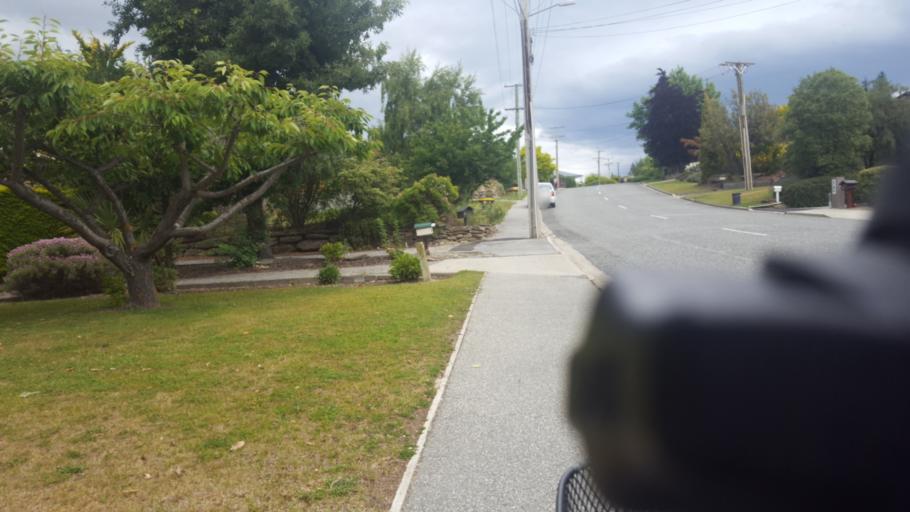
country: NZ
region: Otago
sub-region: Queenstown-Lakes District
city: Wanaka
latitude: -45.2608
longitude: 169.3798
